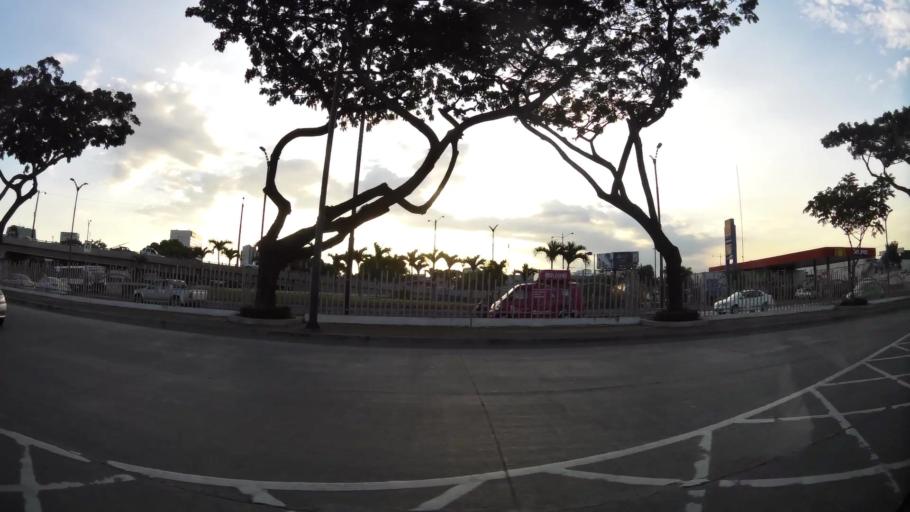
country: EC
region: Guayas
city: Eloy Alfaro
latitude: -2.1637
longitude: -79.8913
